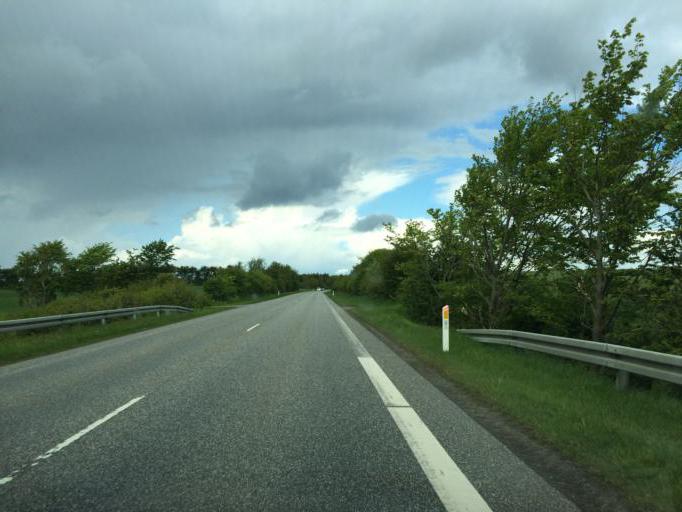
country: DK
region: North Denmark
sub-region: Vesthimmerland Kommune
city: Farso
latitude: 56.7107
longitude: 9.2794
